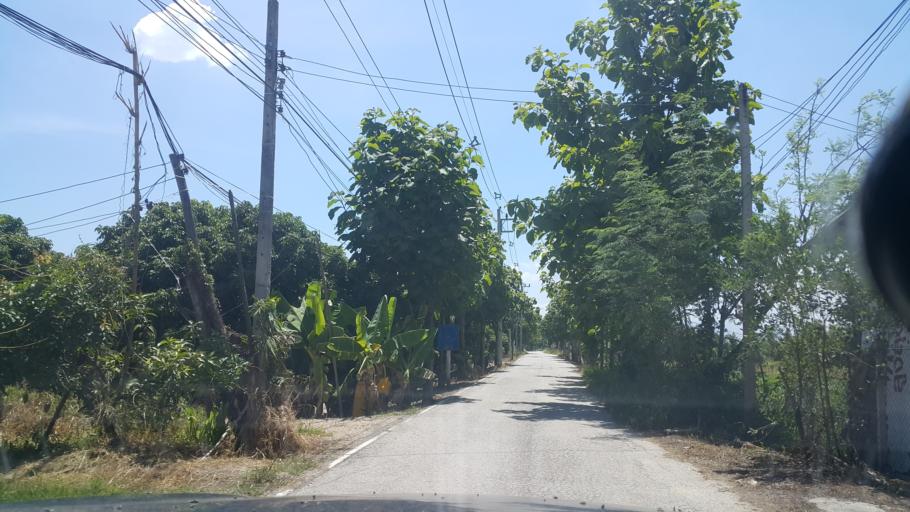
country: TH
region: Chiang Mai
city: San Kamphaeng
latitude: 18.7044
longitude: 99.1554
